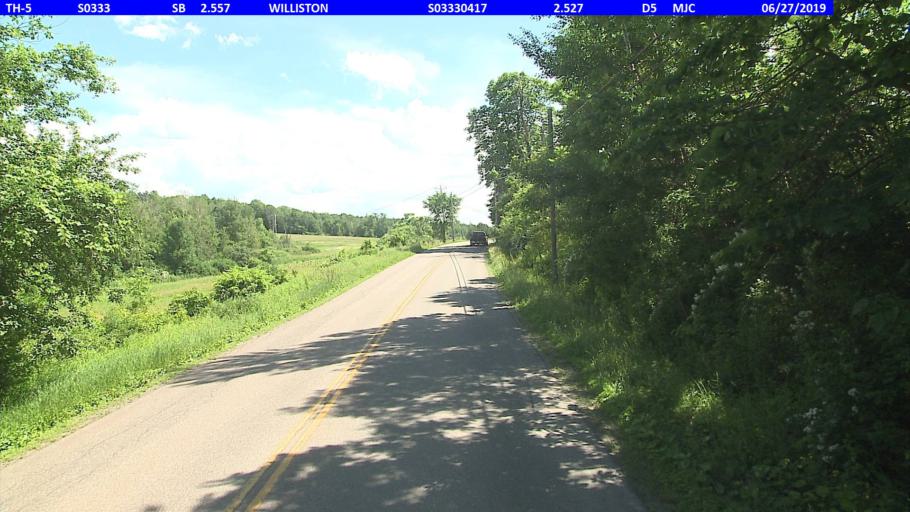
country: US
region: Vermont
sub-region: Chittenden County
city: South Burlington
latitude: 44.4374
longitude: -73.1313
